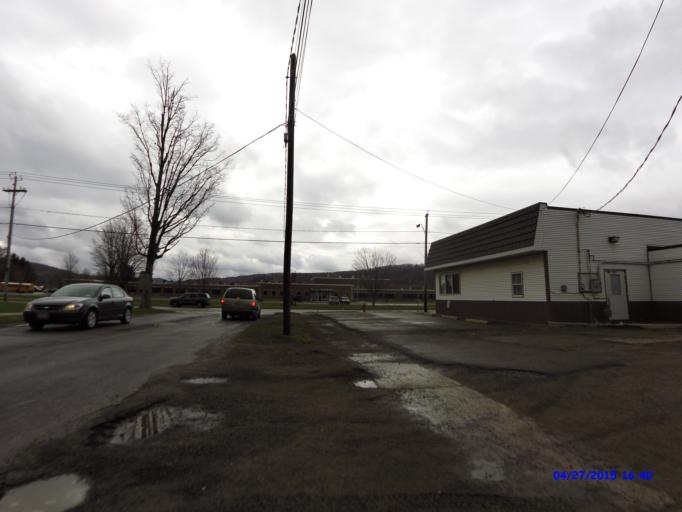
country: US
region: New York
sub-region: Cattaraugus County
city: Franklinville
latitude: 42.3407
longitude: -78.4560
